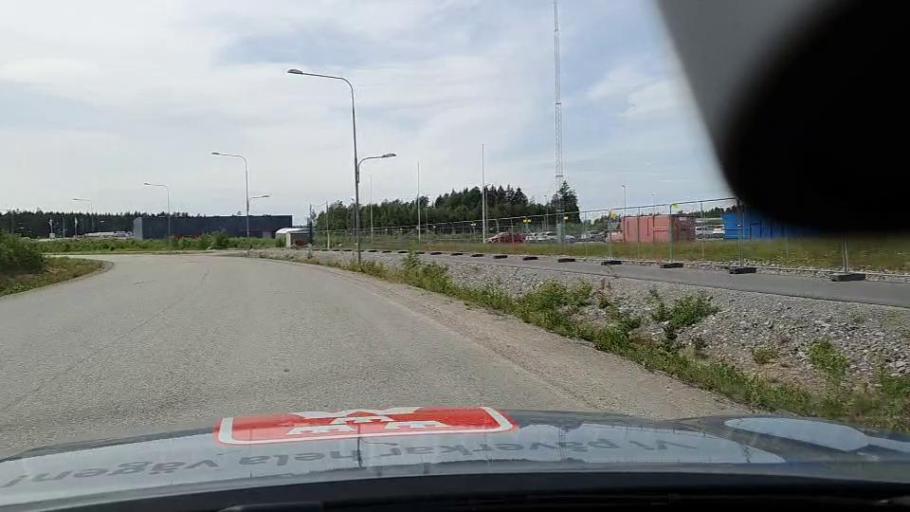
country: SE
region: Soedermanland
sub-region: Eskilstuna Kommun
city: Arla
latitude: 59.3657
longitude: 16.6939
